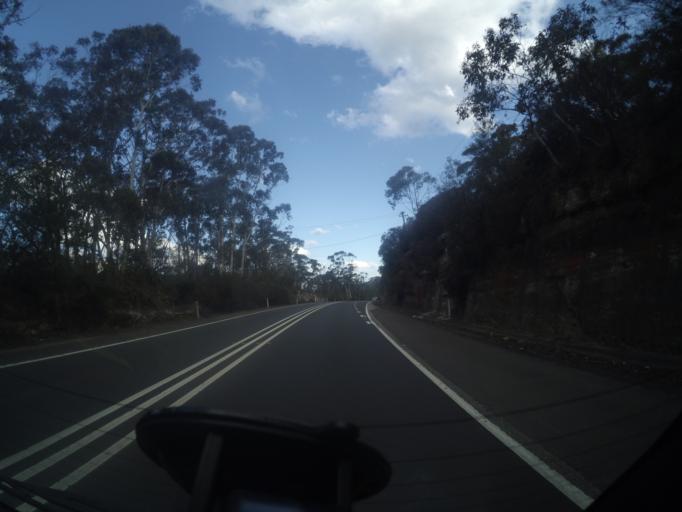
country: AU
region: New South Wales
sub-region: Blue Mountains Municipality
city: Katoomba
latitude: -33.6870
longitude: 150.2894
